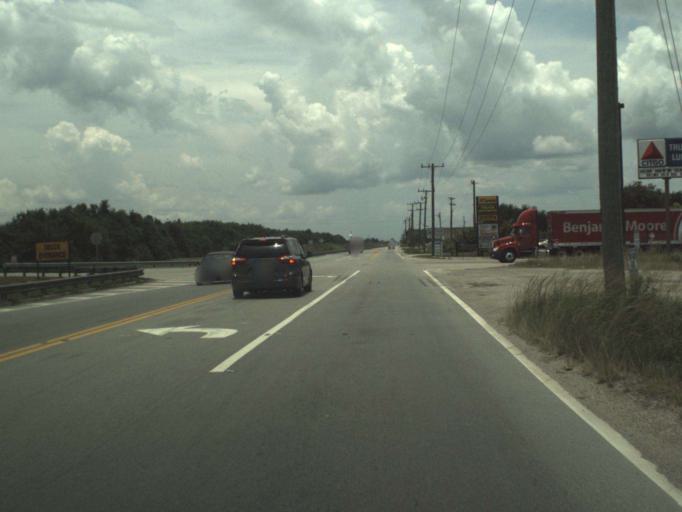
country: US
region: Florida
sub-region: Saint Lucie County
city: Fort Pierce South
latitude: 27.4140
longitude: -80.3991
